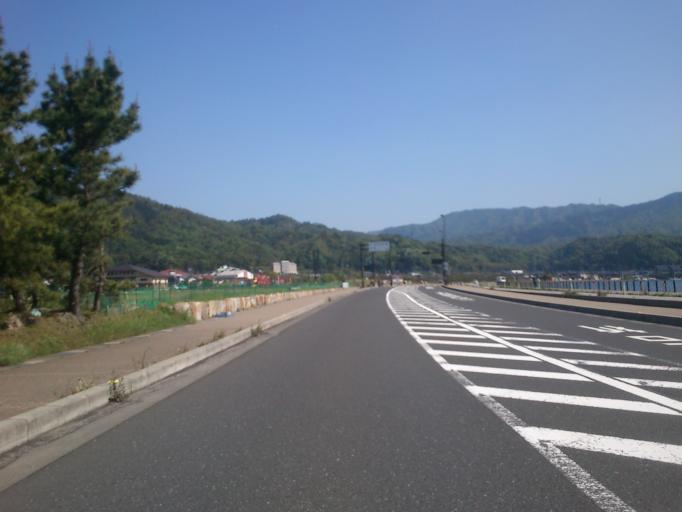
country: JP
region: Kyoto
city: Miyazu
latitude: 35.5636
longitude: 135.1556
